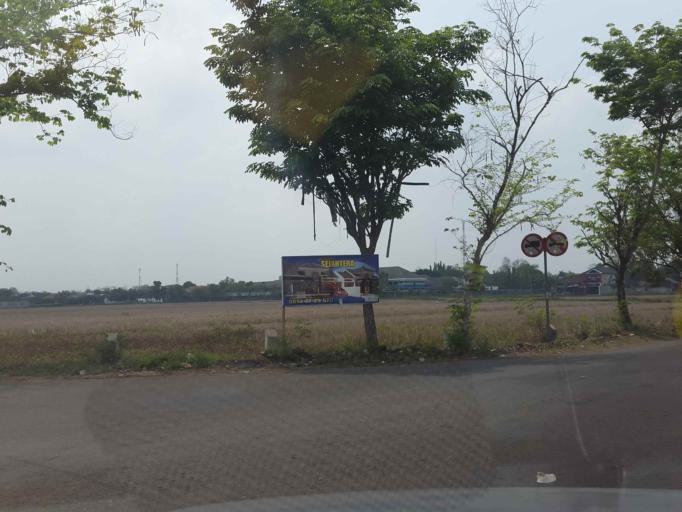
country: ID
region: Central Java
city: Jaten
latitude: -7.5863
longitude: 110.9499
